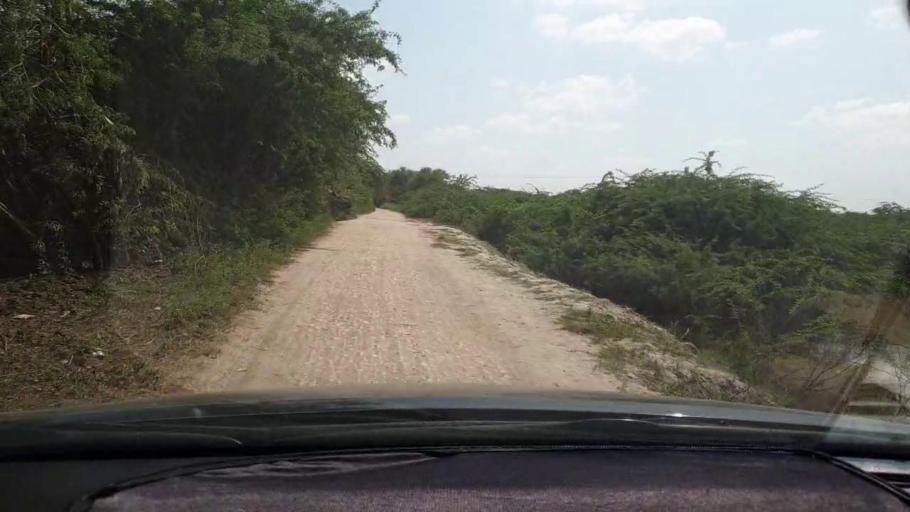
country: PK
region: Sindh
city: Naukot
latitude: 24.9132
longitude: 69.2587
